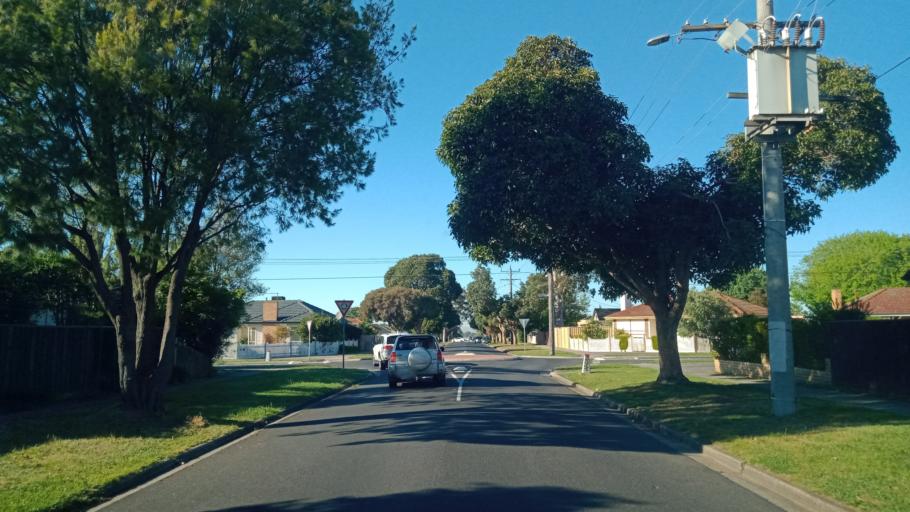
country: AU
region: Victoria
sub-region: Greater Dandenong
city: Springvale
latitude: -37.9371
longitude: 145.1712
